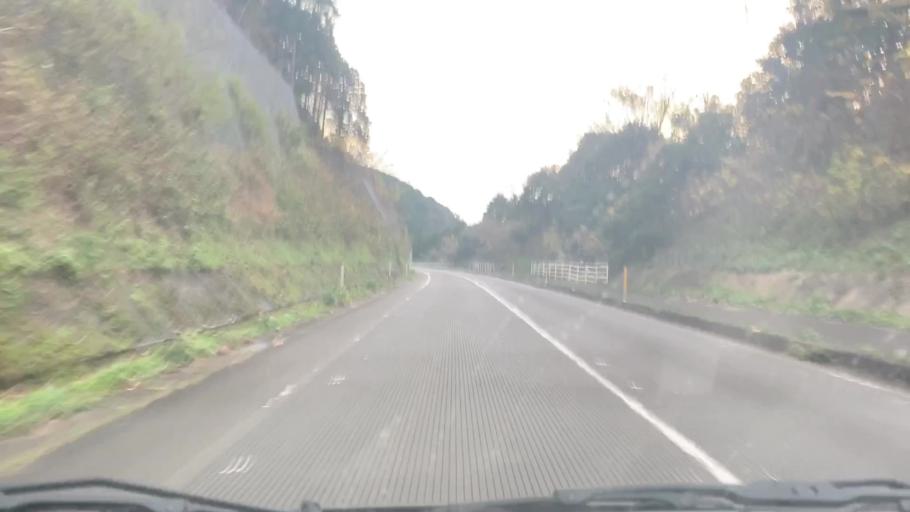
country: JP
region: Saga Prefecture
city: Kashima
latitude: 33.0454
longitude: 130.0717
